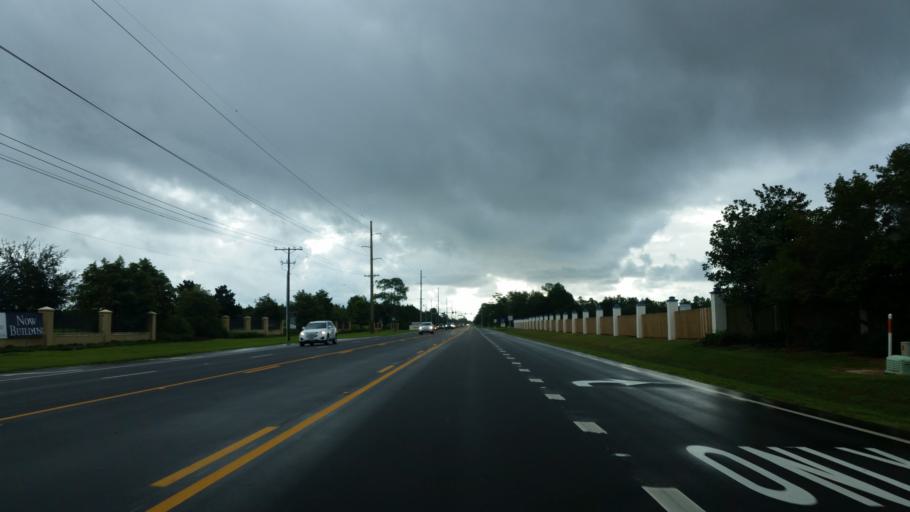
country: US
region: Alabama
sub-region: Baldwin County
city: Orange Beach
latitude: 30.2902
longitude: -87.6182
